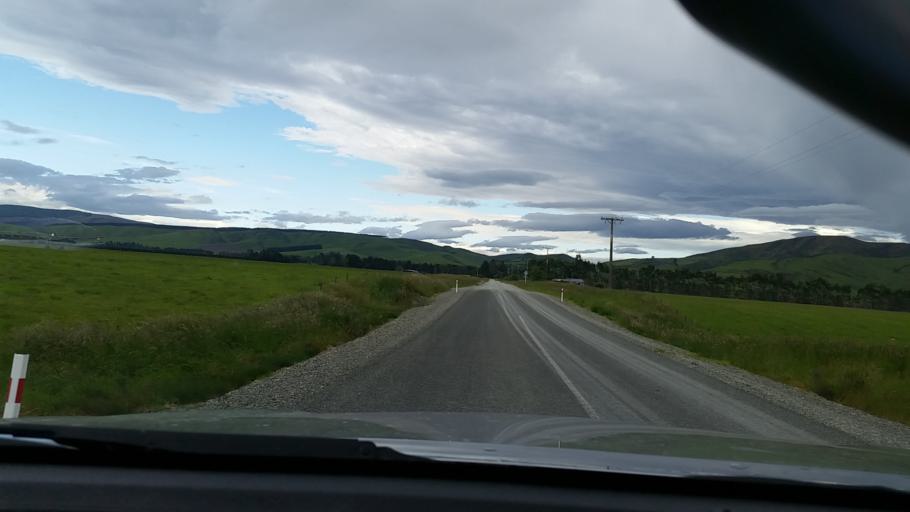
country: NZ
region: Southland
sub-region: Southland District
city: Winton
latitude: -45.8450
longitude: 168.3652
